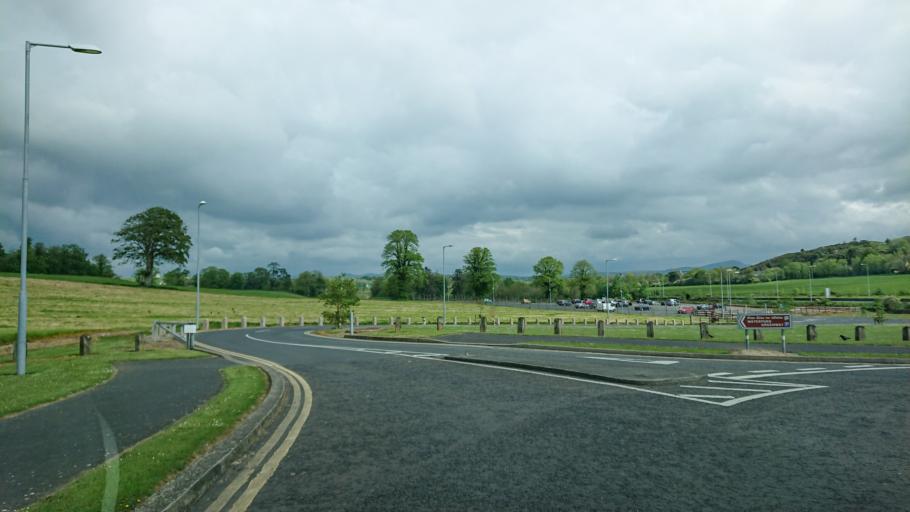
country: IE
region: Munster
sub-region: Waterford
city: Waterford
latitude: 52.2527
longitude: -7.1809
